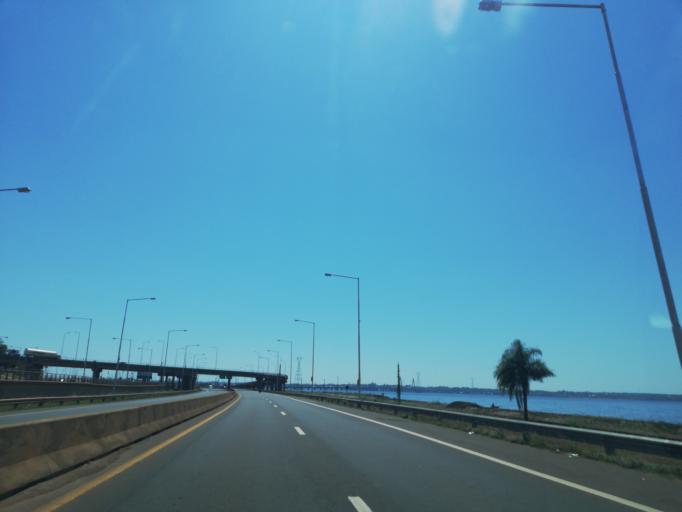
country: AR
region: Misiones
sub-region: Departamento de Capital
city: Posadas
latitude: -27.3871
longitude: -55.8880
